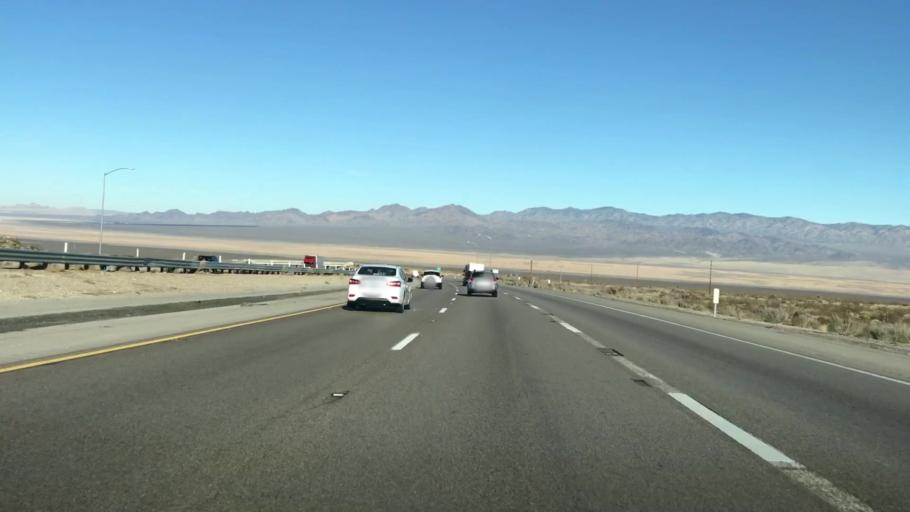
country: US
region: Nevada
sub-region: Clark County
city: Sandy Valley
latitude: 35.4690
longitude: -115.4530
